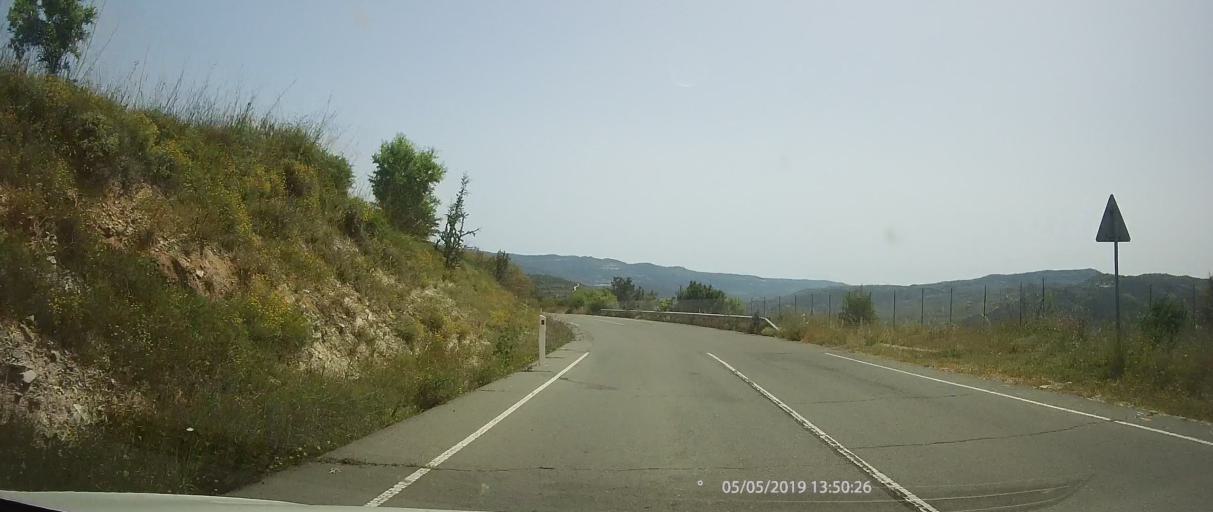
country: CY
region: Limassol
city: Pachna
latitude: 34.8434
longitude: 32.7382
